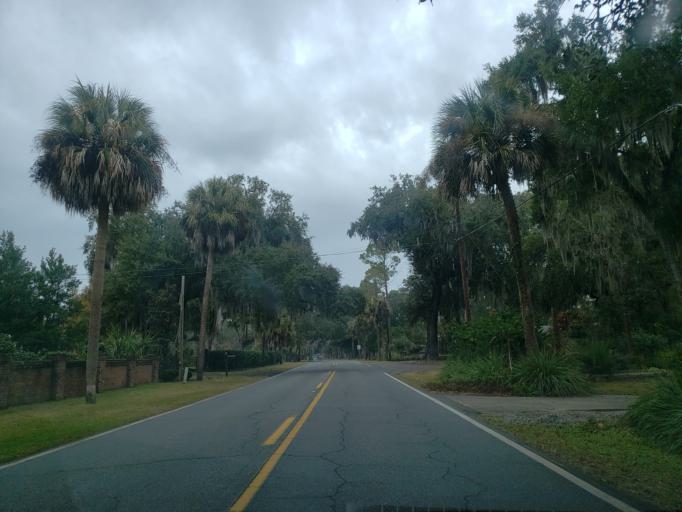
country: US
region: Georgia
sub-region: Chatham County
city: Wilmington Island
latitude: 31.9972
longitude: -80.9956
